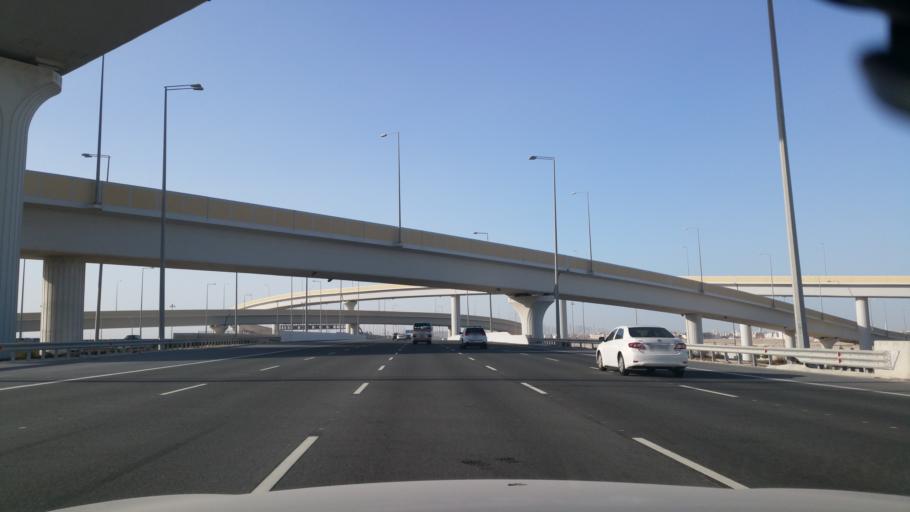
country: QA
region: Al Wakrah
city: Al Wukayr
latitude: 25.2026
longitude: 51.5419
